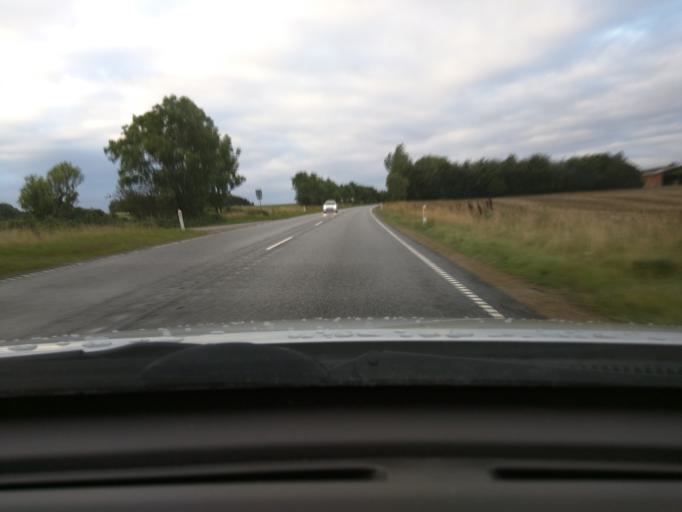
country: DK
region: Central Jutland
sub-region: Viborg Kommune
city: Viborg
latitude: 56.3815
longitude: 9.3804
